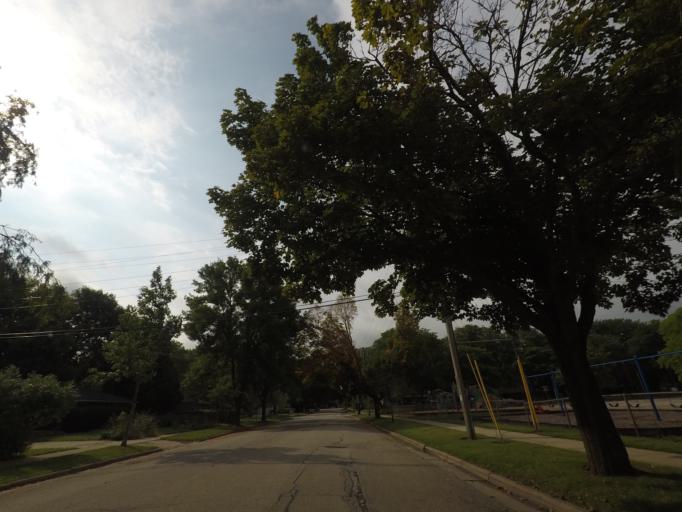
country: US
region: Wisconsin
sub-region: Dane County
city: Shorewood Hills
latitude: 43.0339
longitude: -89.4734
